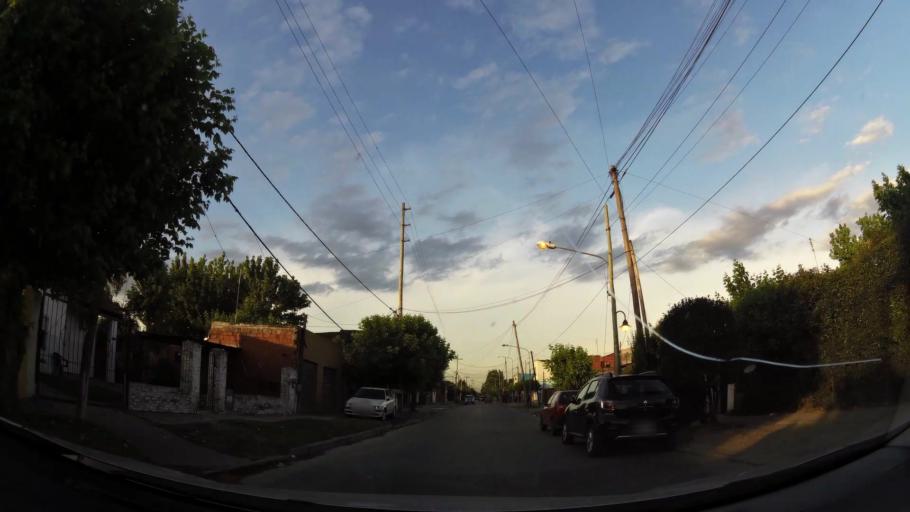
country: AR
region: Buenos Aires
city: Santa Catalina - Dique Lujan
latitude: -34.4488
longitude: -58.6642
